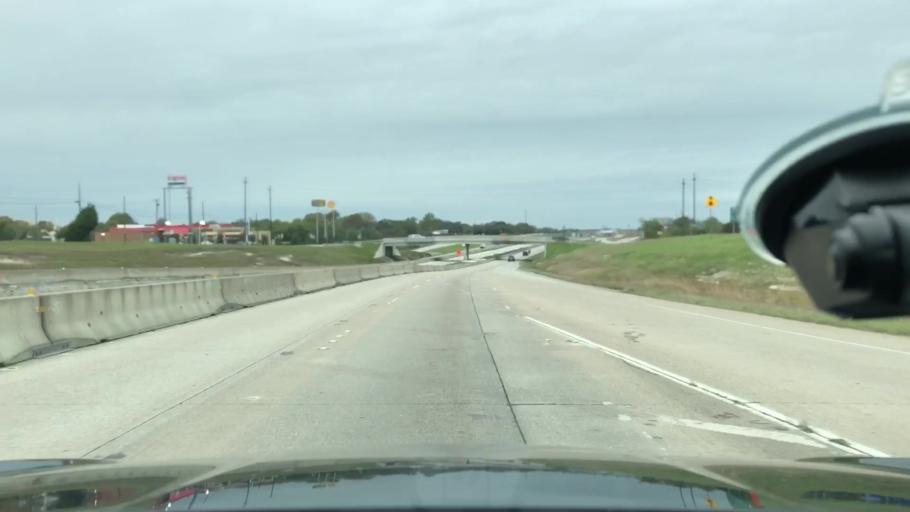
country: US
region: Texas
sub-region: Ellis County
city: Waxahachie
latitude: 32.3724
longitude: -96.8621
